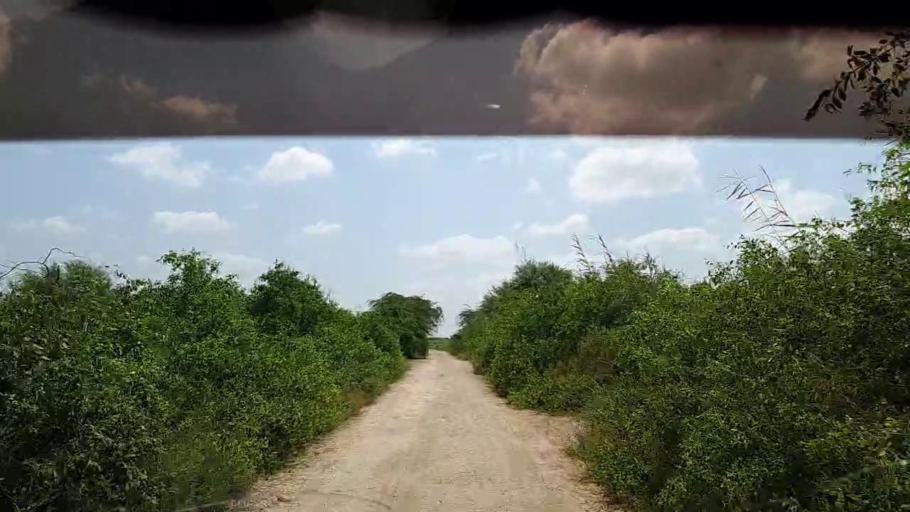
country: PK
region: Sindh
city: Kadhan
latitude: 24.5875
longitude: 68.9585
